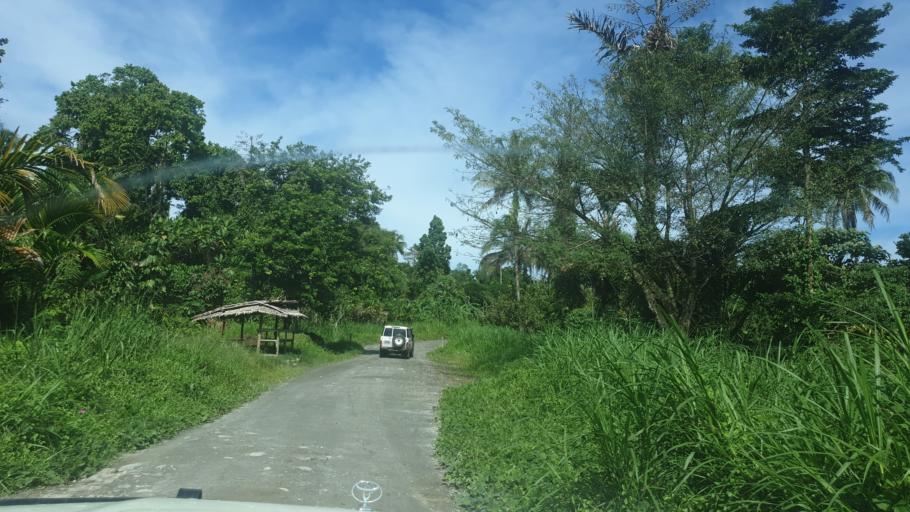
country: PG
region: Bougainville
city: Panguna
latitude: -6.5016
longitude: 155.3299
